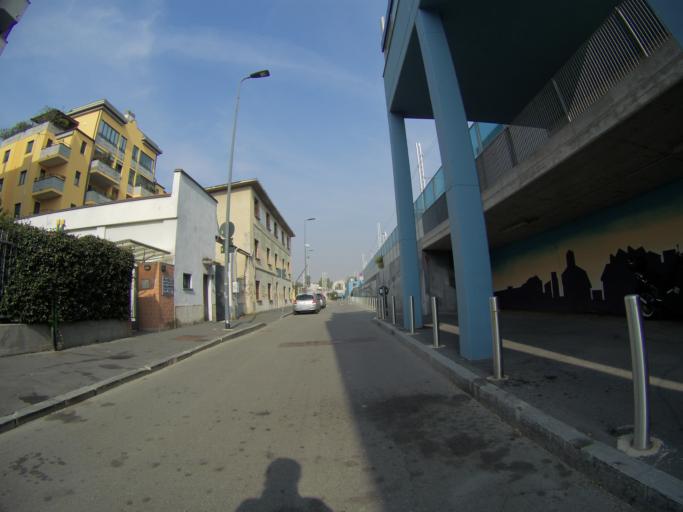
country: IT
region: Lombardy
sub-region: Citta metropolitana di Milano
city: Linate
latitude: 45.4633
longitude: 9.2368
